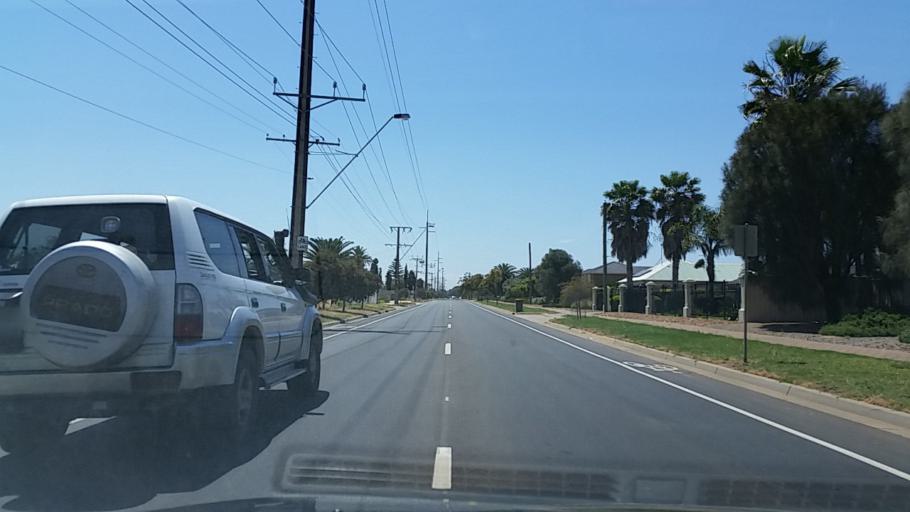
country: AU
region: South Australia
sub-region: Salisbury
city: Salisbury
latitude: -34.7879
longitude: 138.6027
